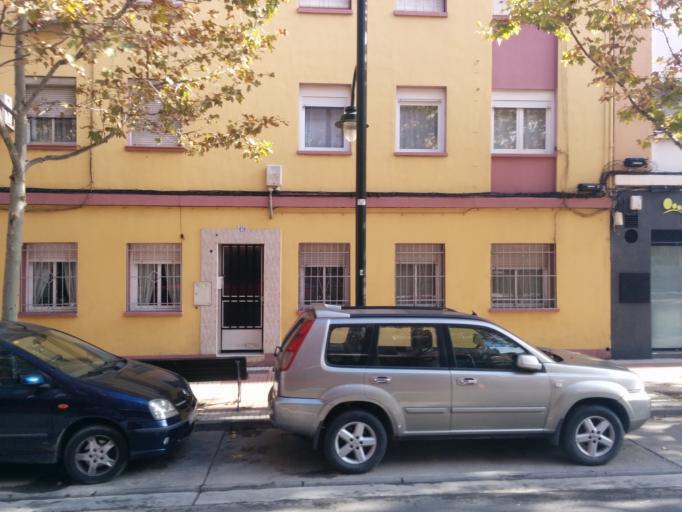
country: ES
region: Aragon
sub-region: Provincia de Zaragoza
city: Delicias
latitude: 41.6292
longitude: -0.8875
